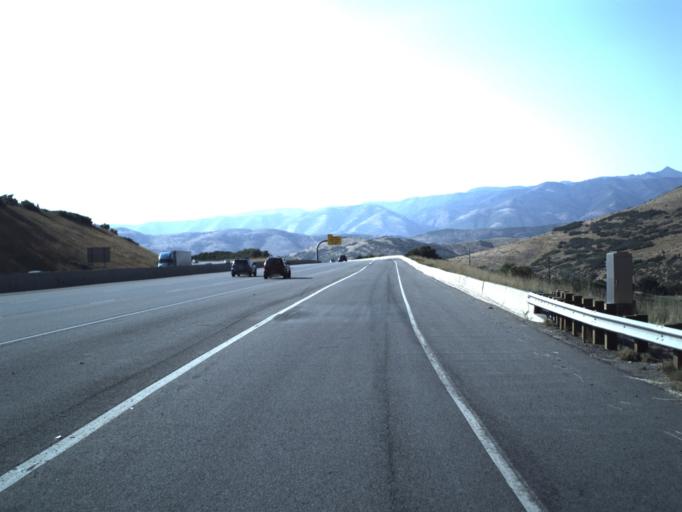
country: US
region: Utah
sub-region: Summit County
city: Summit Park
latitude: 40.7405
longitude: -111.6746
